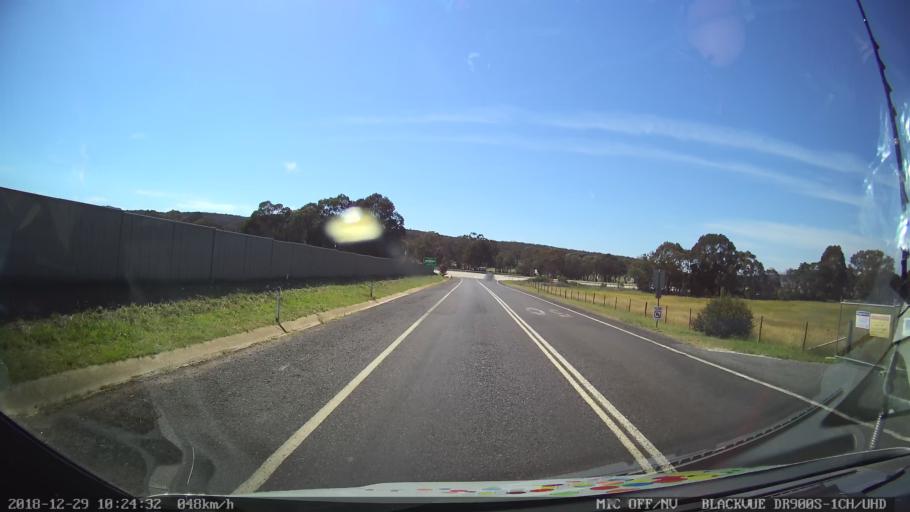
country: AU
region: New South Wales
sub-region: Yass Valley
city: Gundaroo
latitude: -34.9137
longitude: 149.4390
